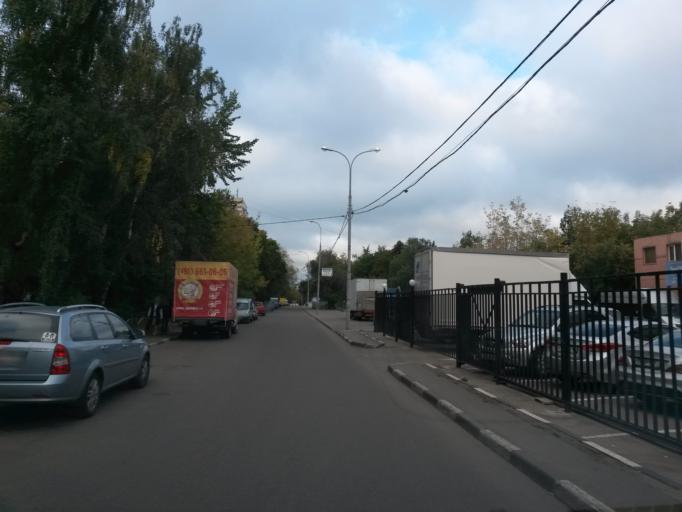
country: RU
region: Moskovskaya
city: Alekseyevka
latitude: 55.6375
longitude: 37.8016
